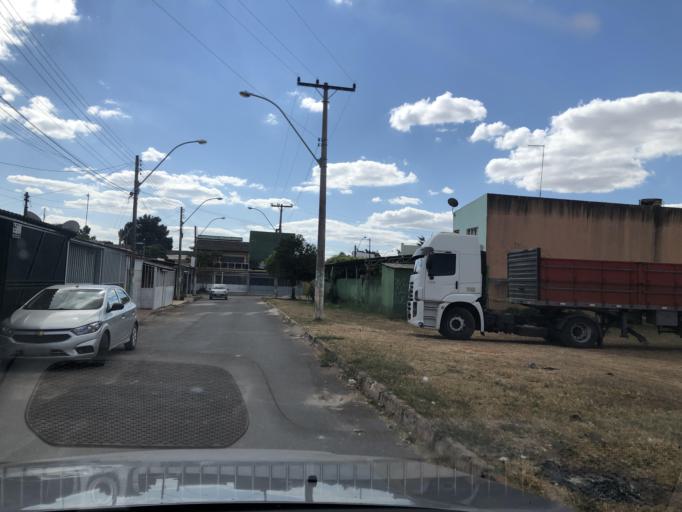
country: BR
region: Federal District
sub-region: Brasilia
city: Brasilia
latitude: -15.8937
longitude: -48.1394
